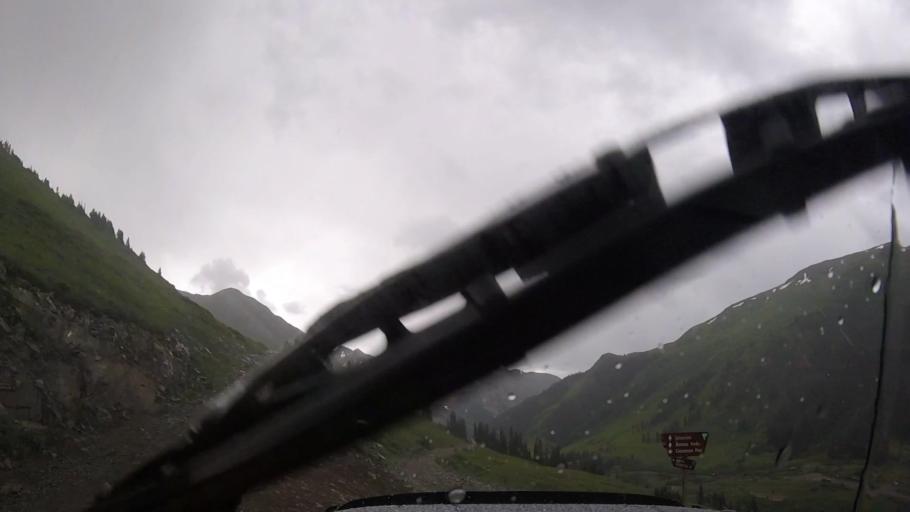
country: US
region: Colorado
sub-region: Ouray County
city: Ouray
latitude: 37.9338
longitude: -107.5686
